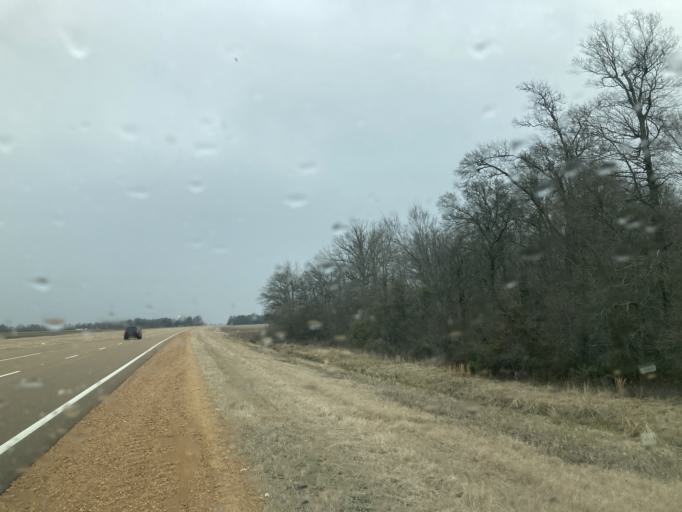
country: US
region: Mississippi
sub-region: Humphreys County
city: Belzoni
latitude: 33.0824
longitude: -90.4835
